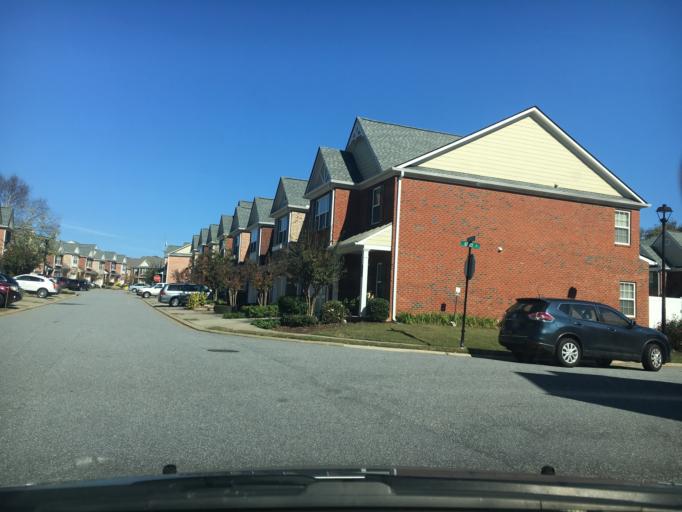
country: US
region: Georgia
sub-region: Fulton County
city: Johns Creek
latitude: 34.0197
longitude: -84.1963
